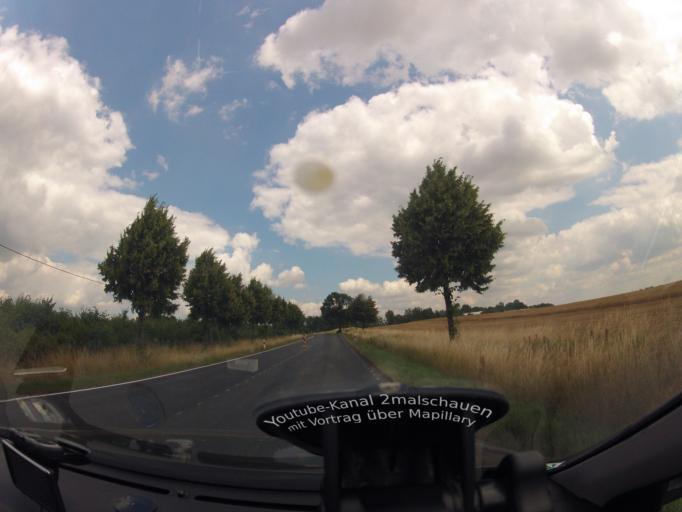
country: DE
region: Saxony
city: Taucha
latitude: 51.3978
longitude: 12.5257
